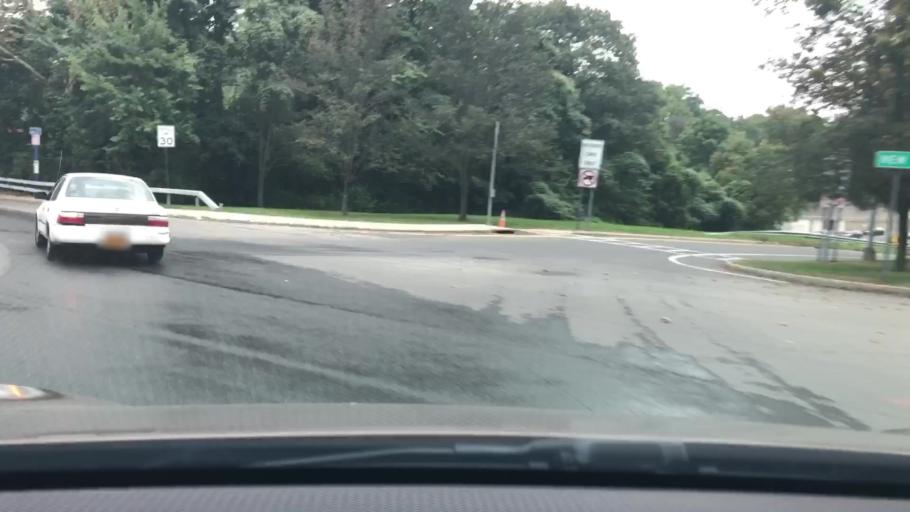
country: US
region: New York
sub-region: Westchester County
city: Pelham
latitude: 40.9294
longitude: -73.8117
